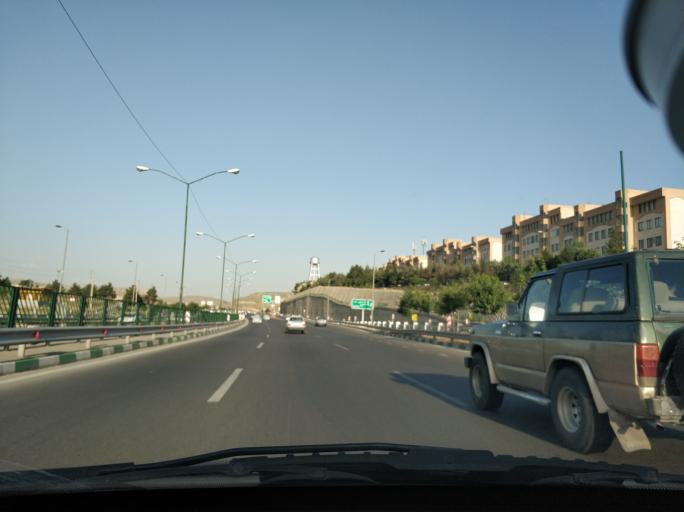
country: IR
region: Tehran
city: Tajrish
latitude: 35.7455
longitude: 51.6001
